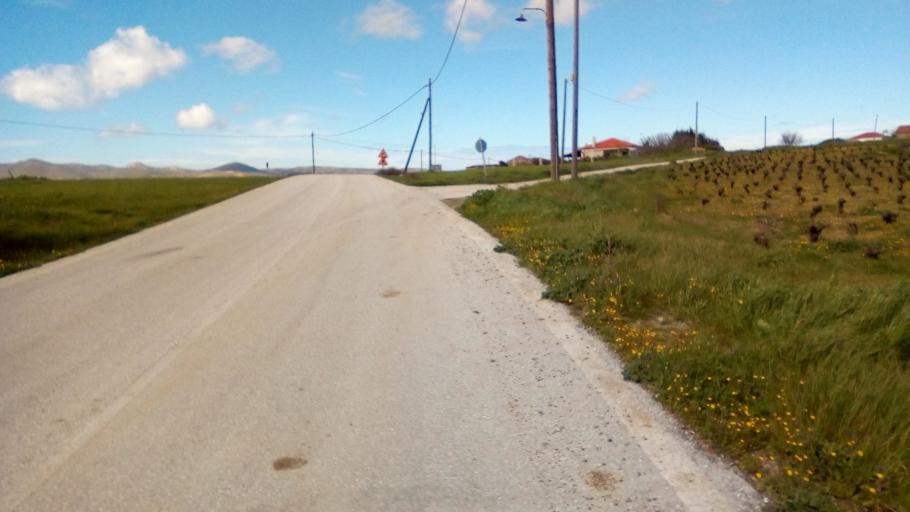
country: GR
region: North Aegean
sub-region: Nomos Lesvou
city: Myrina
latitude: 39.9300
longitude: 25.2317
